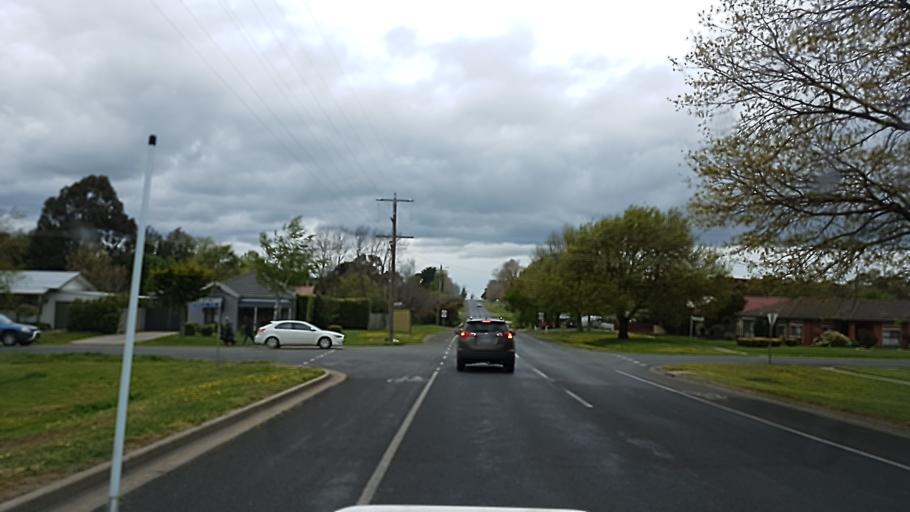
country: AU
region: Victoria
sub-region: Moorabool
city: Bacchus Marsh
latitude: -37.6002
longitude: 144.2355
